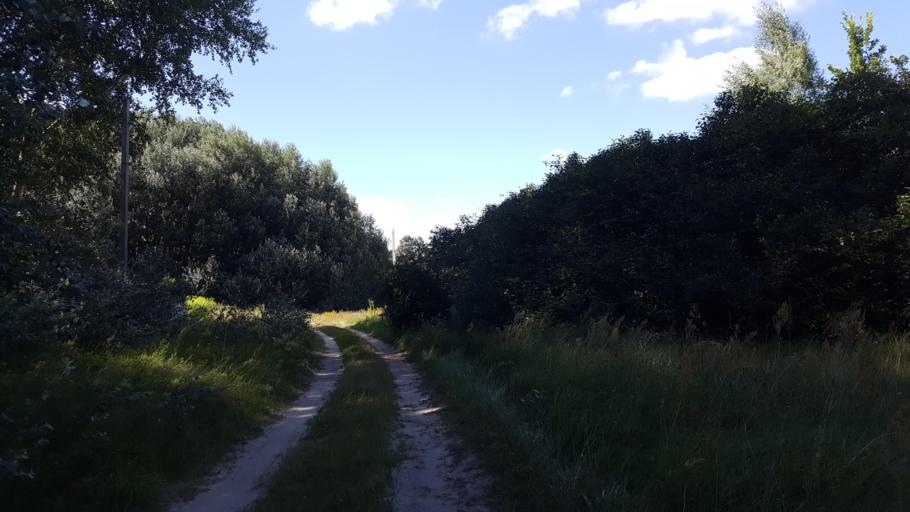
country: BY
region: Brest
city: Kobryn
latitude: 52.3084
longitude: 24.3109
